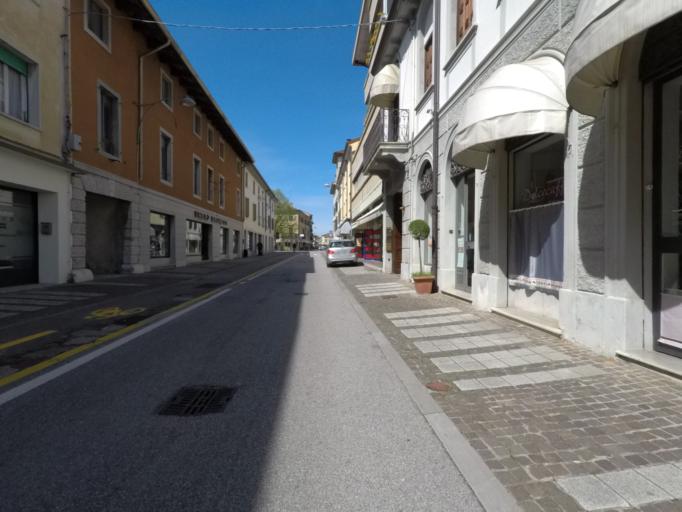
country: IT
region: Friuli Venezia Giulia
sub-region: Provincia di Udine
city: Codroipo
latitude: 45.9609
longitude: 12.9803
